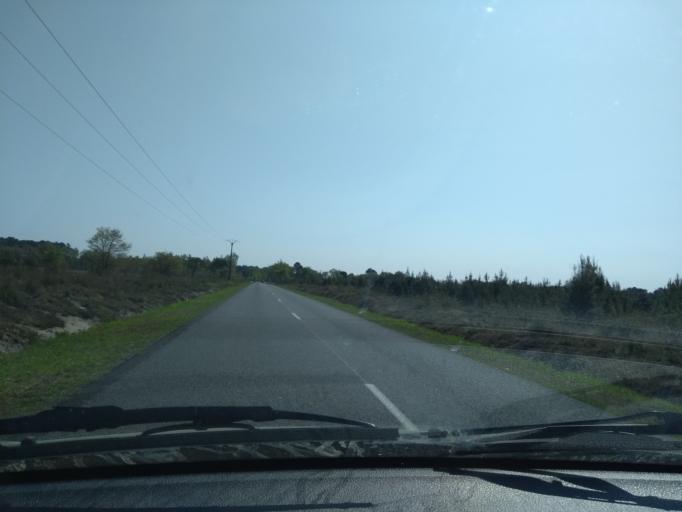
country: FR
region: Aquitaine
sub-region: Departement de la Gironde
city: Belin-Beliet
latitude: 44.5284
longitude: -0.6755
